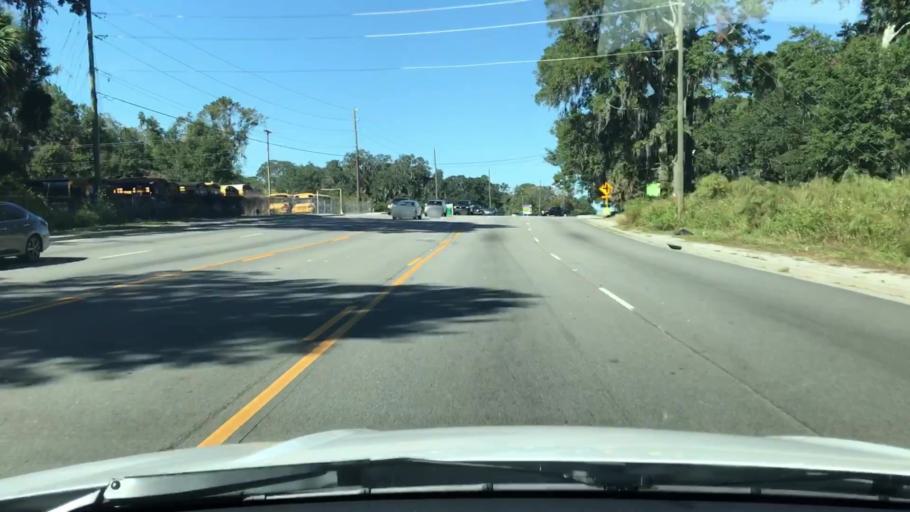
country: US
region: South Carolina
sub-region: Beaufort County
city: Burton
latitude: 32.4512
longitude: -80.7319
